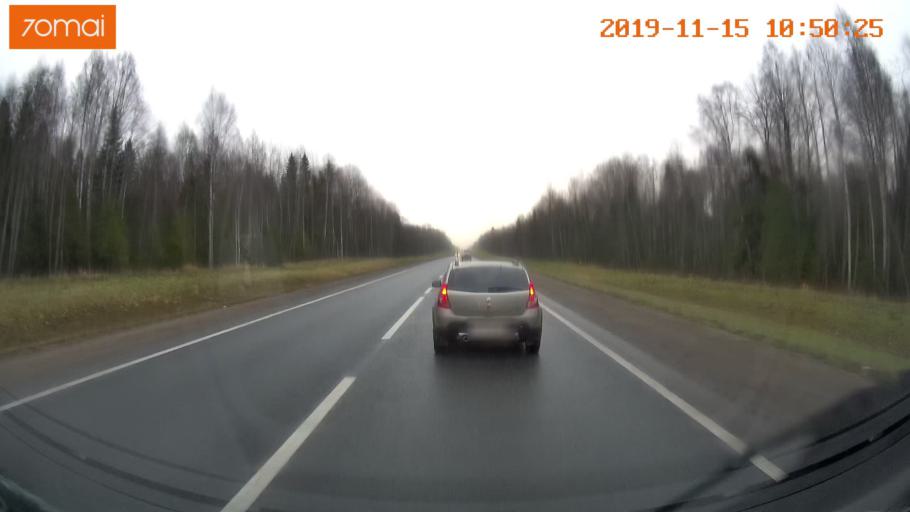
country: RU
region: Vologda
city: Chebsara
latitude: 59.1854
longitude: 38.6813
